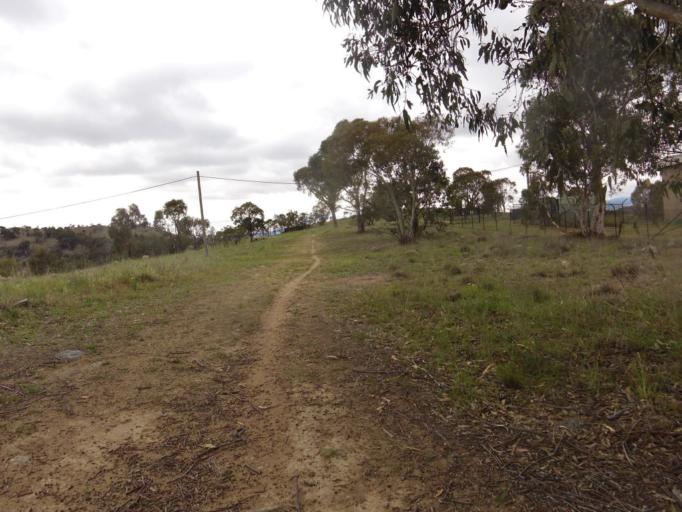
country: AU
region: Australian Capital Territory
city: Macarthur
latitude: -35.3629
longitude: 149.0380
